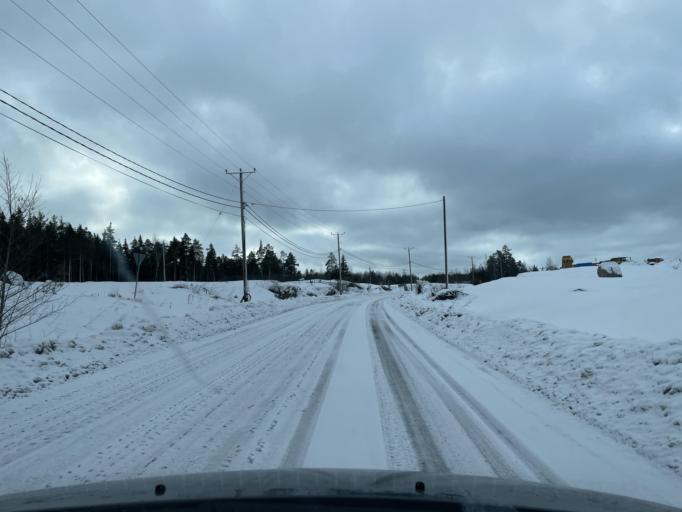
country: FI
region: Uusimaa
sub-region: Helsinki
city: Espoo
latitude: 60.2423
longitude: 24.5602
